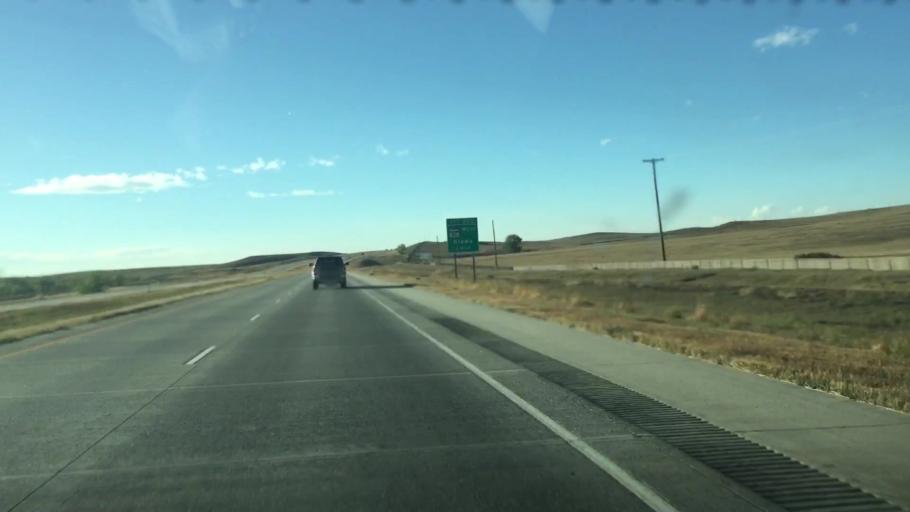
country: US
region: Colorado
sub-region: Lincoln County
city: Limon
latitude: 39.2994
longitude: -103.8093
